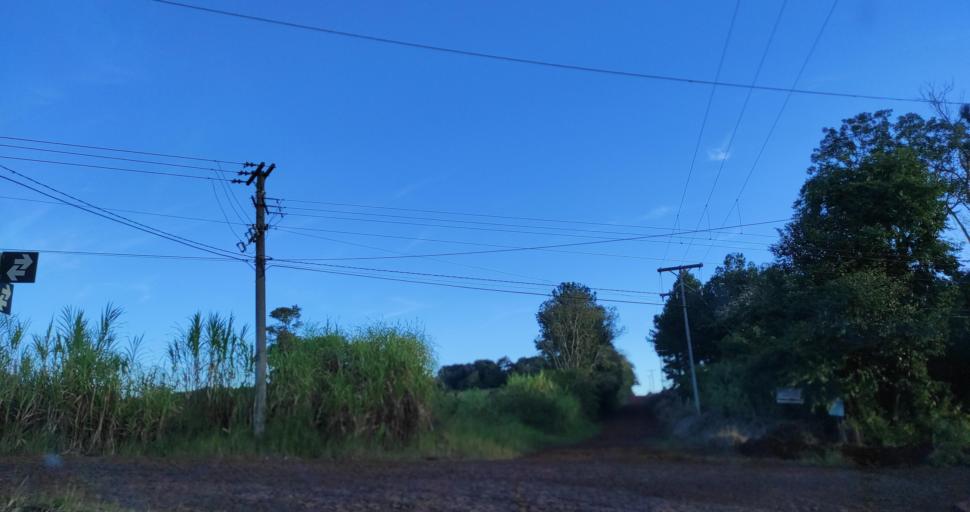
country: AR
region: Misiones
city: Capiovi
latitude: -26.8645
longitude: -55.0486
